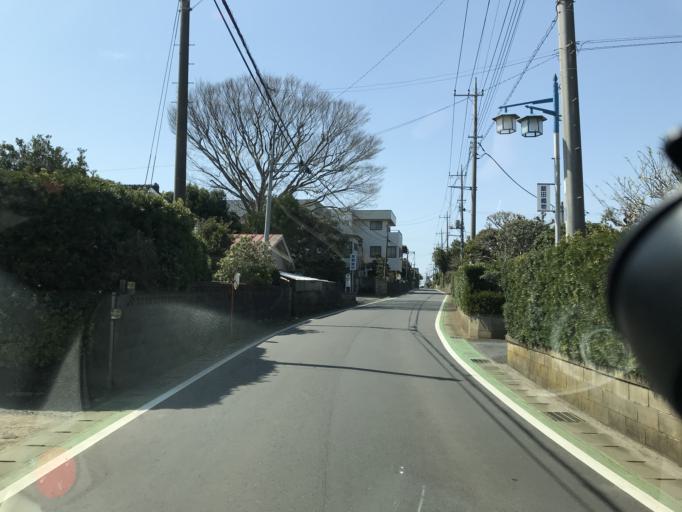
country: JP
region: Chiba
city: Asahi
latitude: 35.7905
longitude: 140.6831
